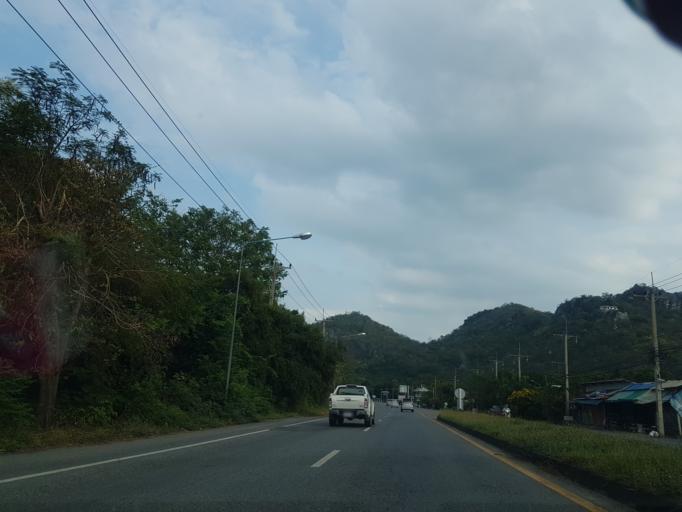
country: TH
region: Sara Buri
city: Phra Phutthabat
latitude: 14.7160
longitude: 100.7883
